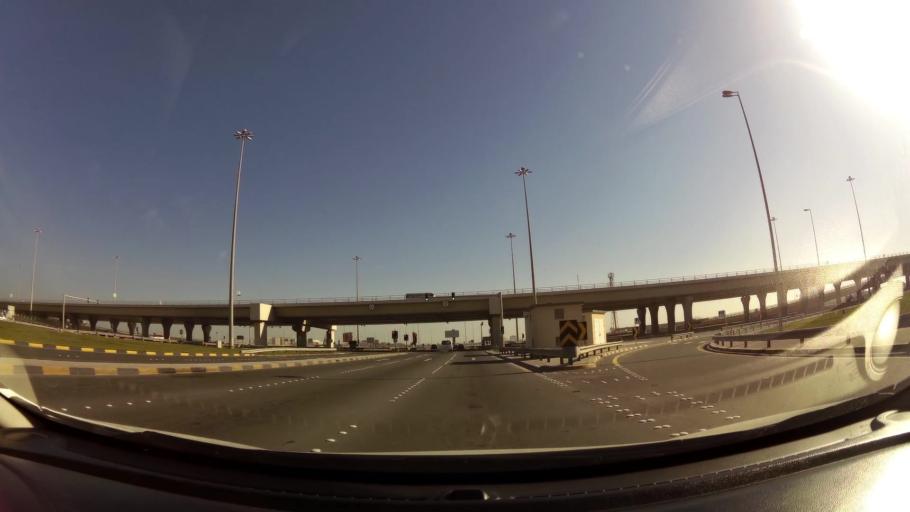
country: BH
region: Muharraq
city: Al Muharraq
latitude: 26.2457
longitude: 50.5891
